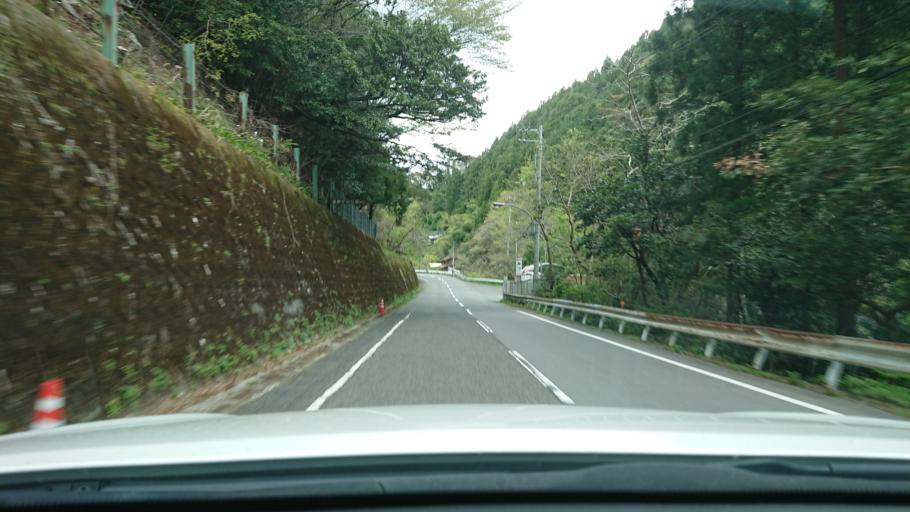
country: JP
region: Tokushima
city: Ishii
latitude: 33.9136
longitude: 134.4207
